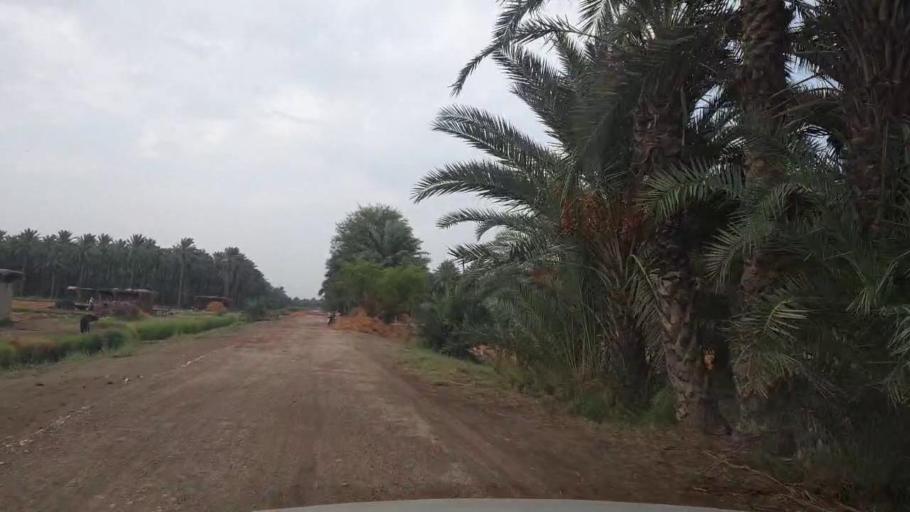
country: PK
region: Sindh
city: Sukkur
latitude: 27.6121
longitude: 68.8359
